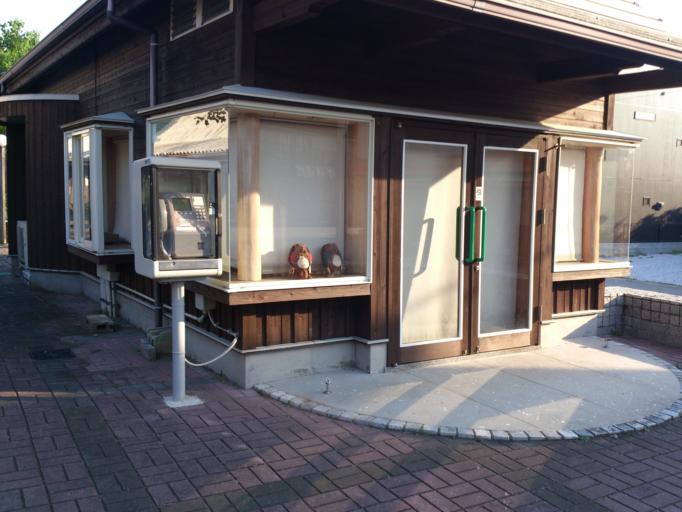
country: JP
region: Chiba
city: Tateyama
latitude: 35.0451
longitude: 139.8377
